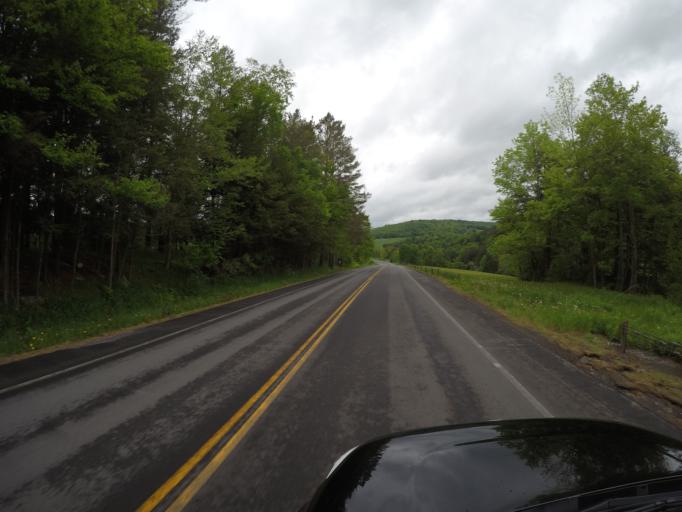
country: US
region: New York
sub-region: Delaware County
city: Delhi
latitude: 42.2464
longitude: -74.8156
